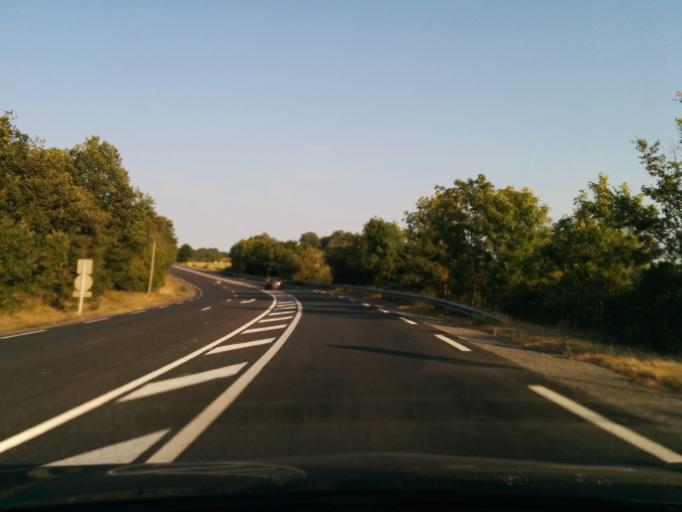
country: FR
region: Midi-Pyrenees
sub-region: Departement du Lot
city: Le Vigan
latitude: 44.6016
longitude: 1.5060
